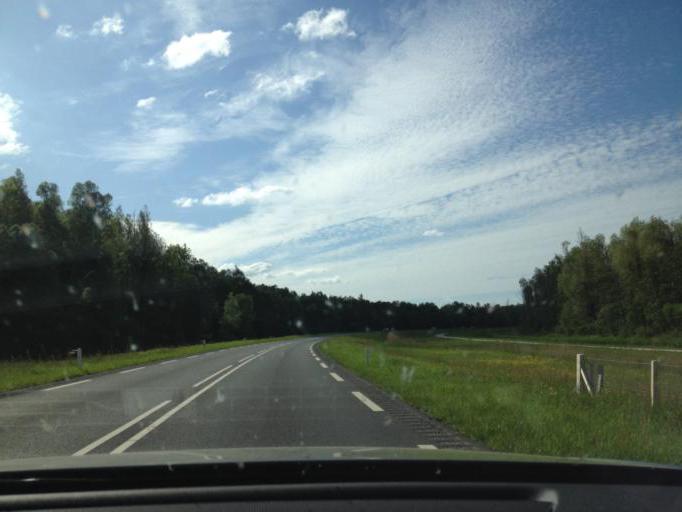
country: NL
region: Gelderland
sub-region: Gemeente Nijkerk
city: Nijkerk
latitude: 52.2633
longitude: 5.4599
